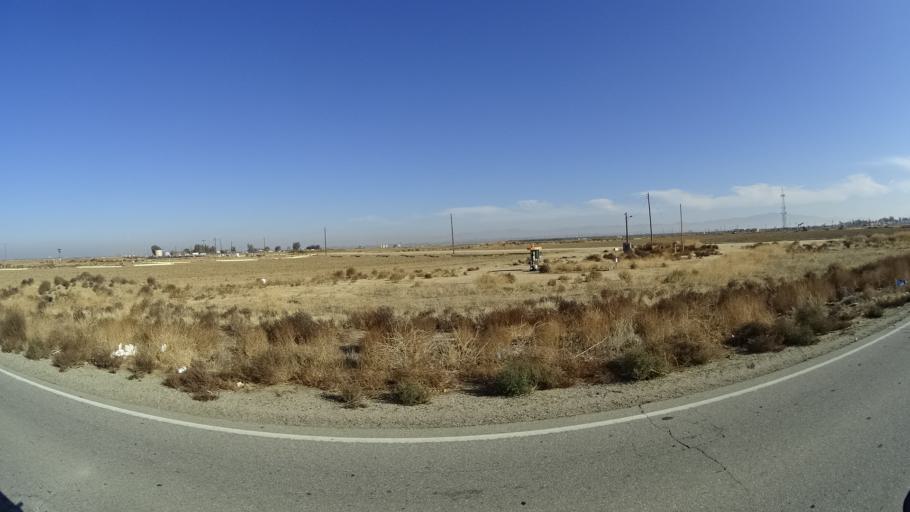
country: US
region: California
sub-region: Kern County
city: Rosedale
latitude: 35.4321
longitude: -119.1508
